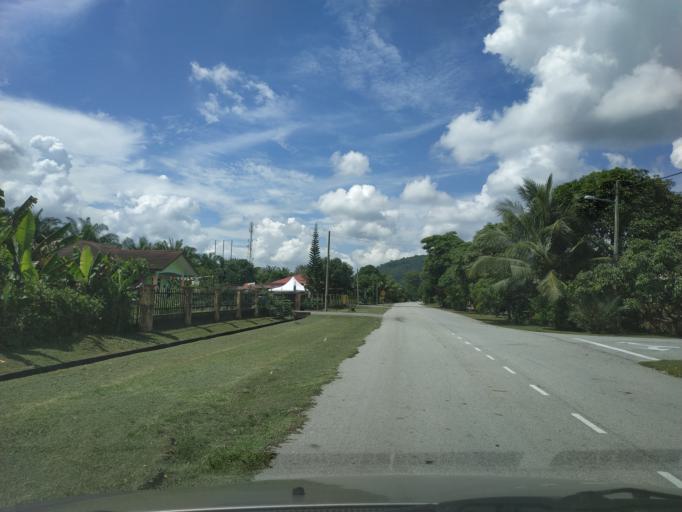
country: MY
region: Perak
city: Parit Buntar
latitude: 5.1385
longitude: 100.5971
